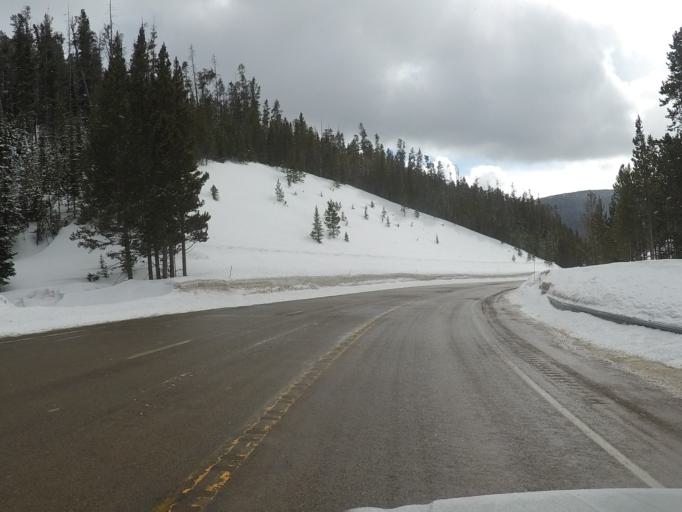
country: US
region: Montana
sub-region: Meagher County
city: White Sulphur Springs
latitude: 46.8258
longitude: -110.6952
